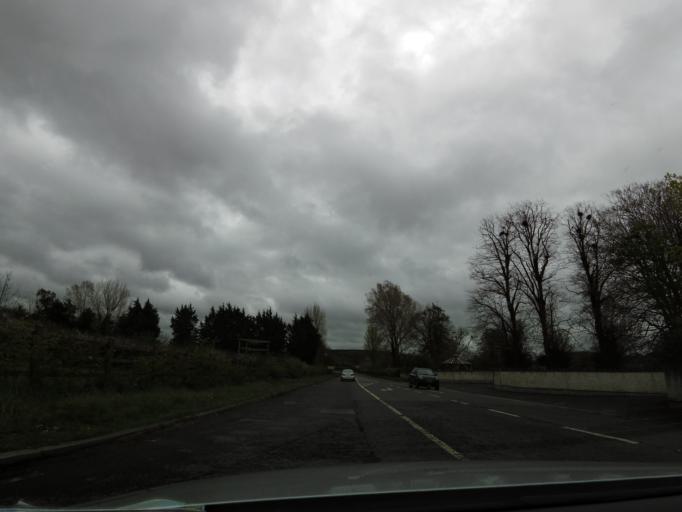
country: IE
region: Leinster
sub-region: Kilkenny
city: Ballyragget
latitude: 52.7118
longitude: -7.3274
